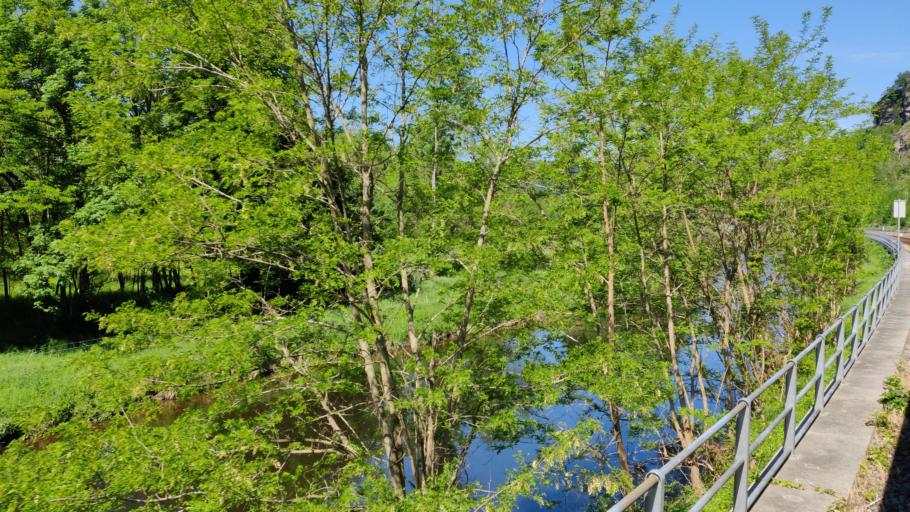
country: AT
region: Lower Austria
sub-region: Politischer Bezirk Horn
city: Gars am Kamp
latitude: 48.5691
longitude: 15.6704
